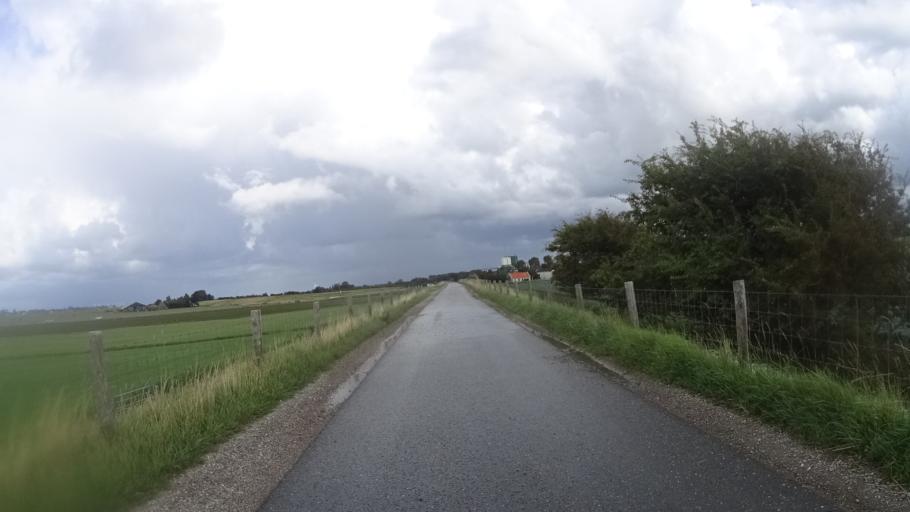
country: NL
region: North Holland
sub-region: Gemeente Schagen
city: Schagen
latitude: 52.7959
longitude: 4.7691
